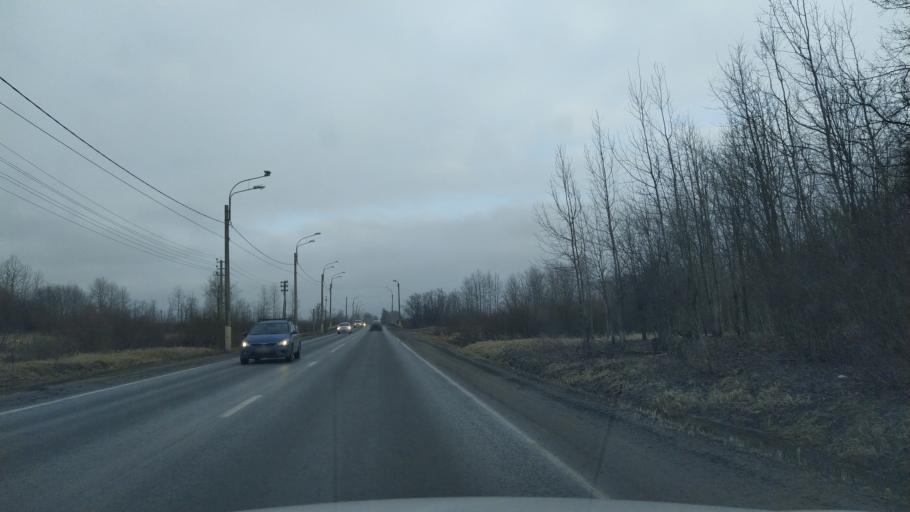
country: RU
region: St.-Petersburg
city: Aleksandrovskaya
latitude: 59.7127
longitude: 30.3082
